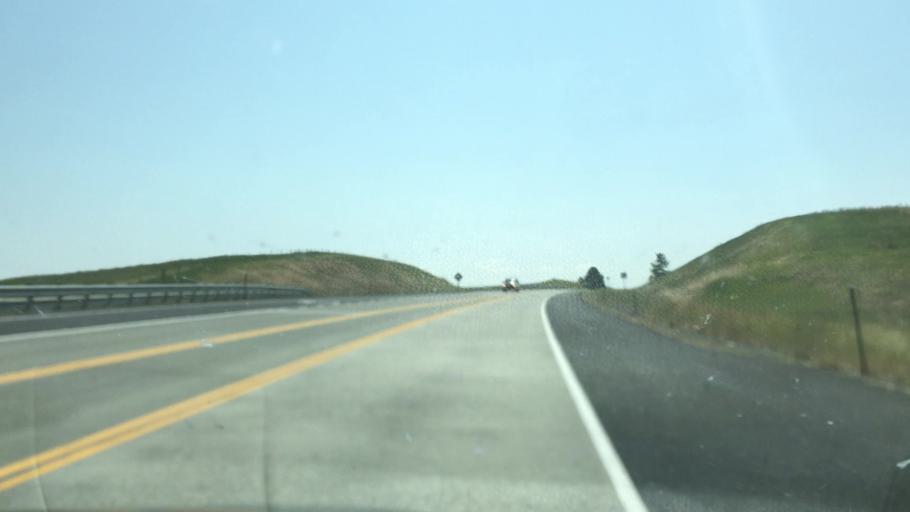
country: US
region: Idaho
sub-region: Lewis County
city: Nezperce
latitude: 46.0985
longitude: -116.3509
